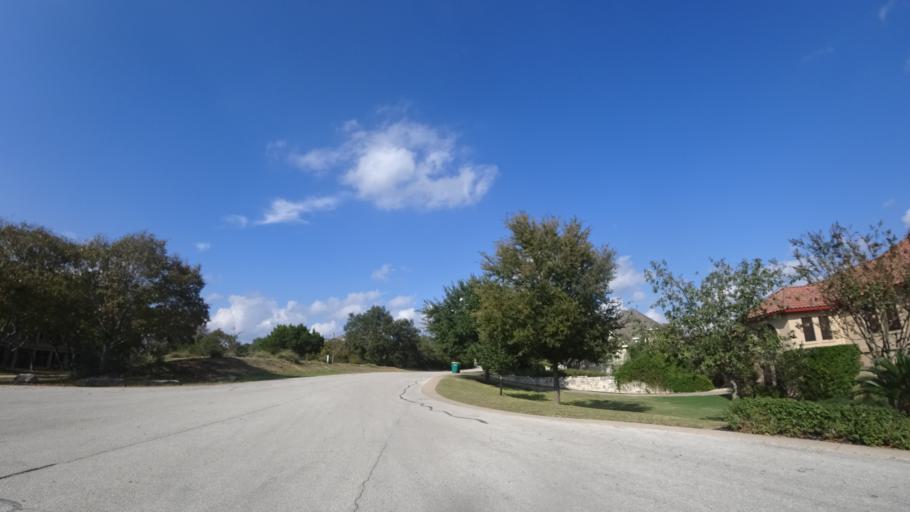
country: US
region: Texas
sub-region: Travis County
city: Lost Creek
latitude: 30.3013
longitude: -97.8507
